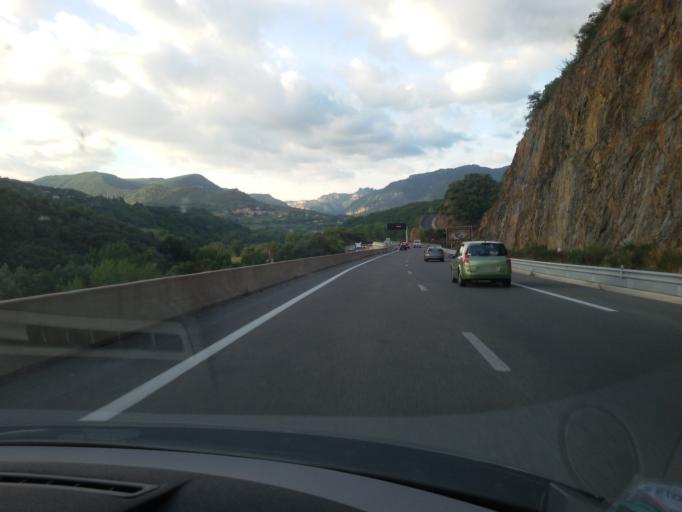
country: FR
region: Languedoc-Roussillon
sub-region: Departement de l'Herault
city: Lodeve
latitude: 43.7415
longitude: 3.3306
